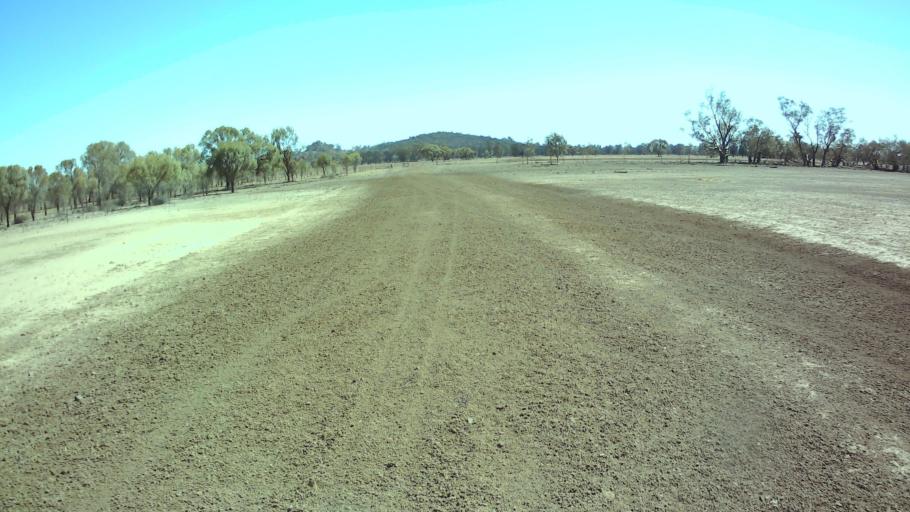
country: AU
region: New South Wales
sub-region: Bland
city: West Wyalong
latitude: -33.7521
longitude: 147.6599
